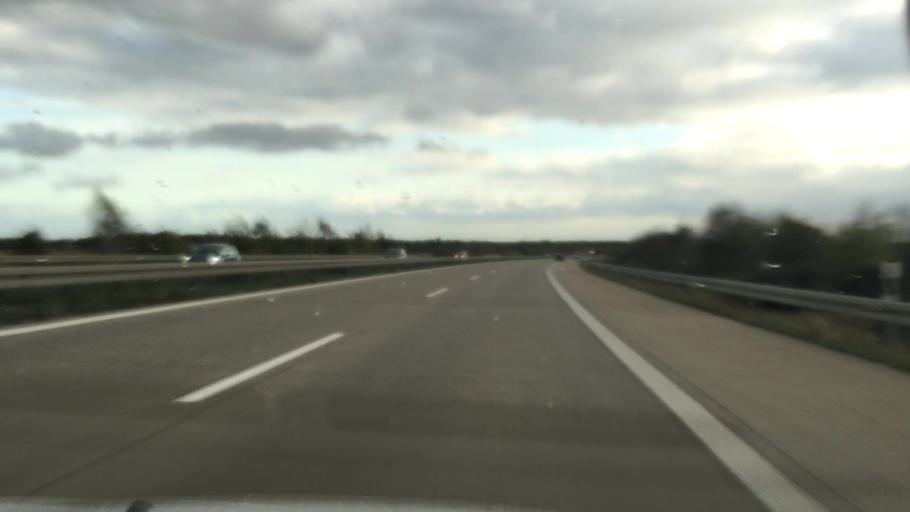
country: DE
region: Saxony-Anhalt
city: Brumby
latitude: 51.8651
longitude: 11.6937
